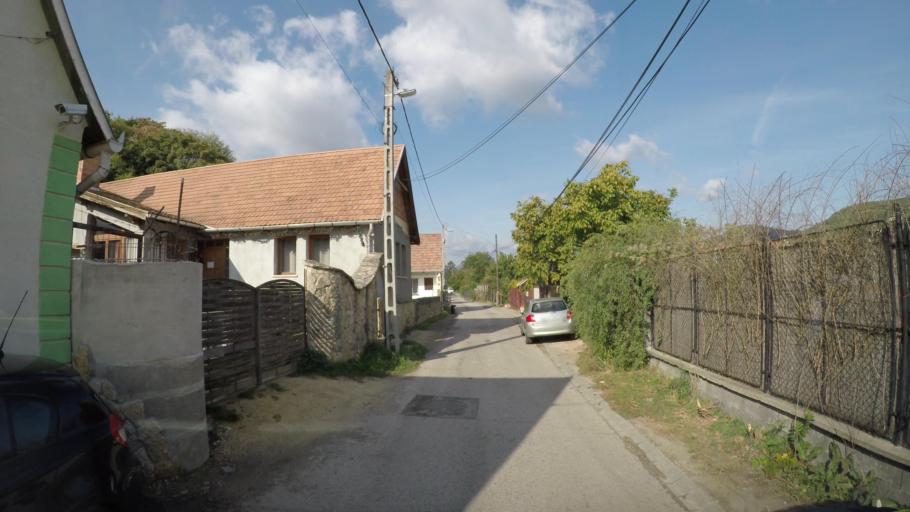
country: HU
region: Pest
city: Nagykovacsi
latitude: 47.6479
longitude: 19.0076
